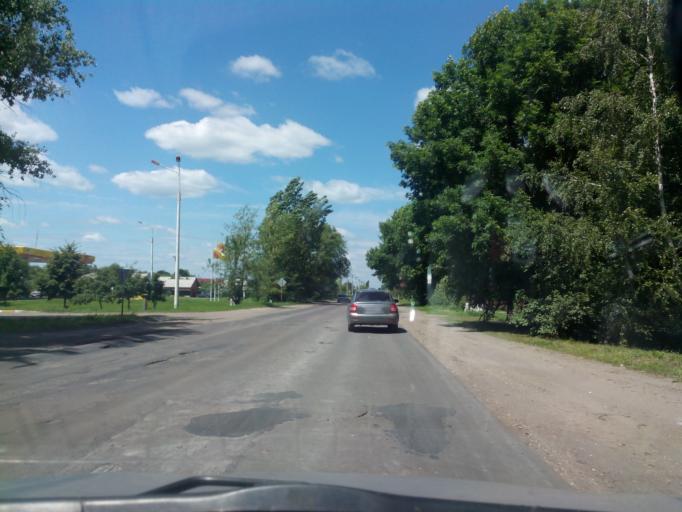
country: RU
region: Tambov
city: Zherdevka
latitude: 51.8217
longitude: 41.5034
